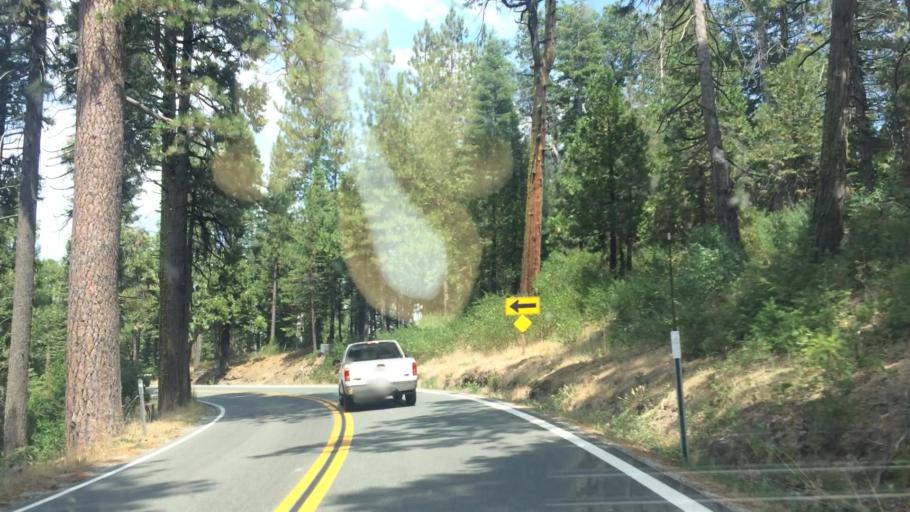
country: US
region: California
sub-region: Amador County
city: Pioneer
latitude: 38.5173
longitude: -120.4577
